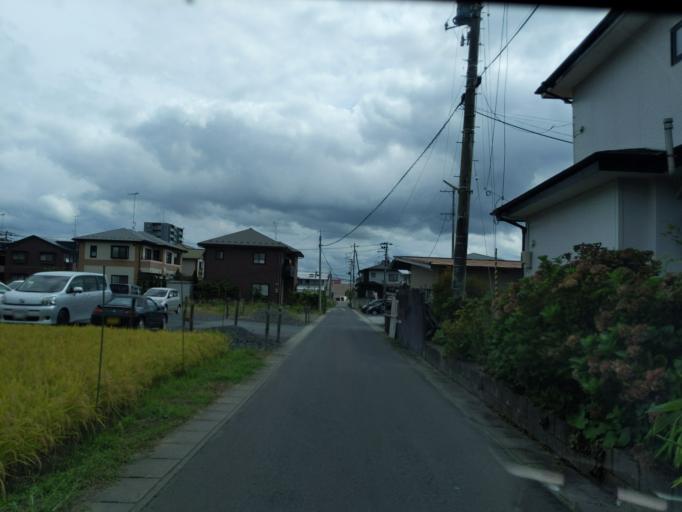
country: JP
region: Iwate
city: Ichinoseki
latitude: 38.9375
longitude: 141.1073
